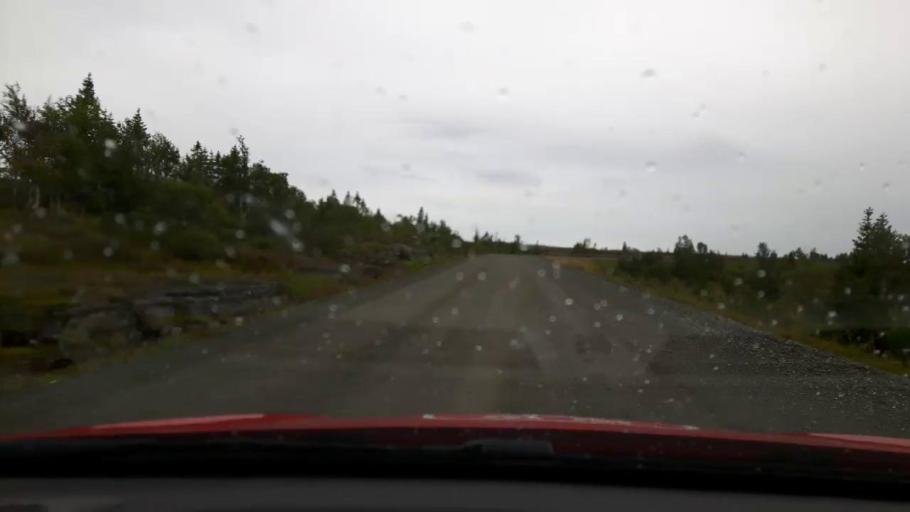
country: NO
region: Nord-Trondelag
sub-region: Meraker
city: Meraker
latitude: 63.6322
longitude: 12.2836
